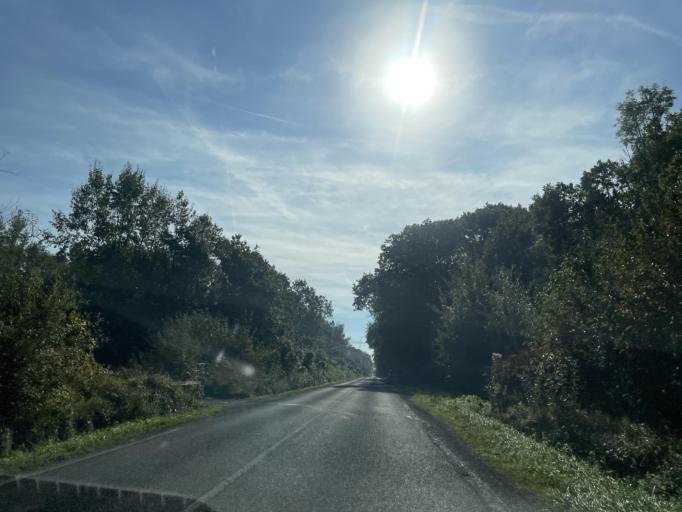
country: FR
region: Ile-de-France
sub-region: Departement de Seine-et-Marne
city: Saint-Jean-les-Deux-Jumeaux
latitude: 48.9535
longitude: 2.9875
